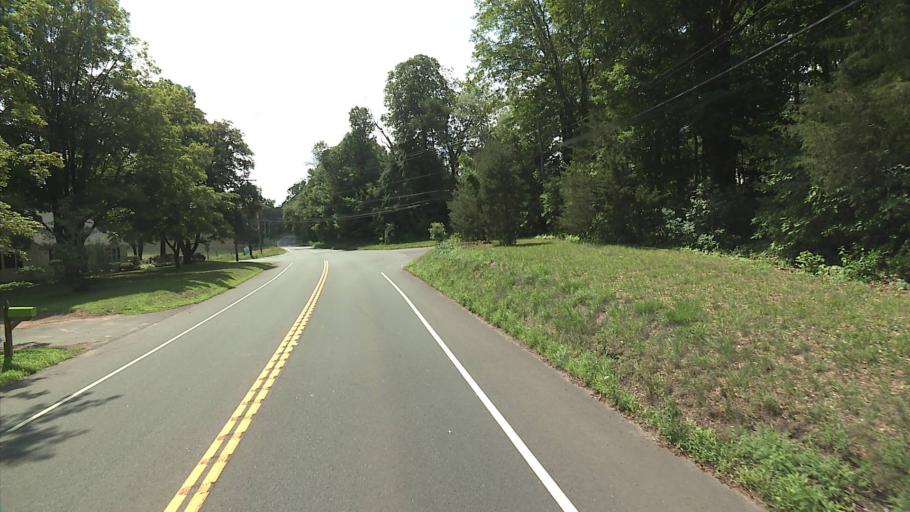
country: US
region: Connecticut
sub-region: Middlesex County
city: Portland
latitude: 41.5812
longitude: -72.6096
